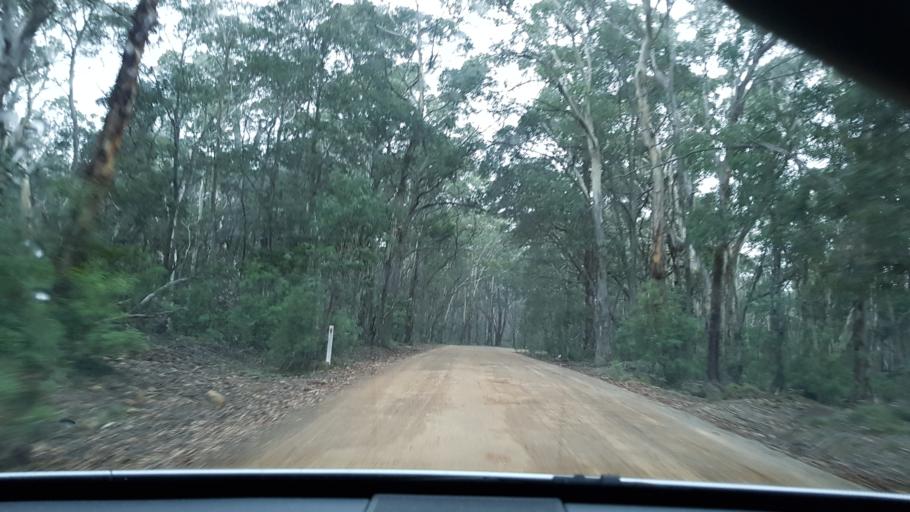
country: AU
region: New South Wales
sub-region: Oberon
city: Oberon
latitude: -33.9795
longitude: 150.0566
